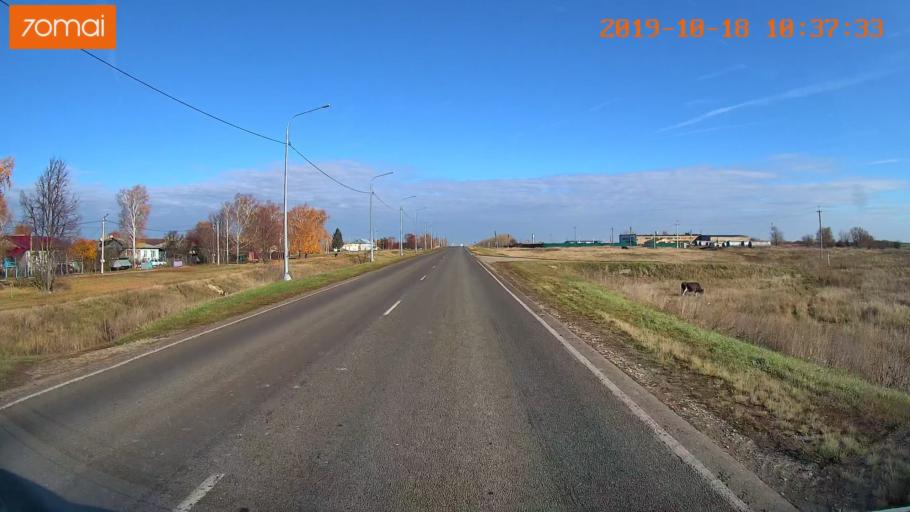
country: RU
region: Tula
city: Kurkino
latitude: 53.5635
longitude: 38.6329
